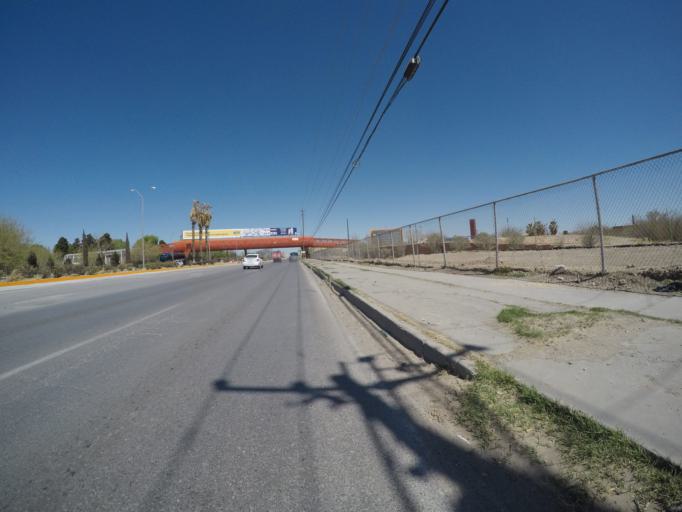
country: MX
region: Chihuahua
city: Ciudad Juarez
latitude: 31.6868
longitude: -106.4243
